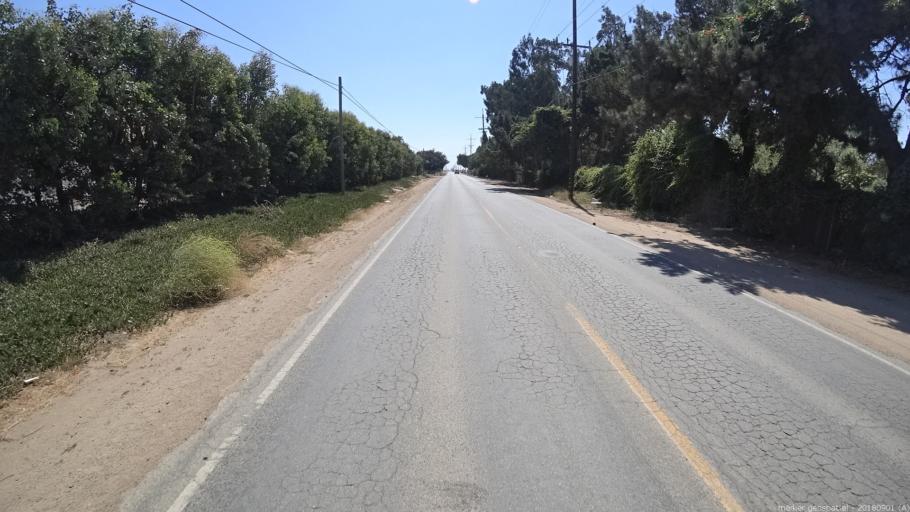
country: US
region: California
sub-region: Monterey County
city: Chualar
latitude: 36.6179
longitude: -121.5236
